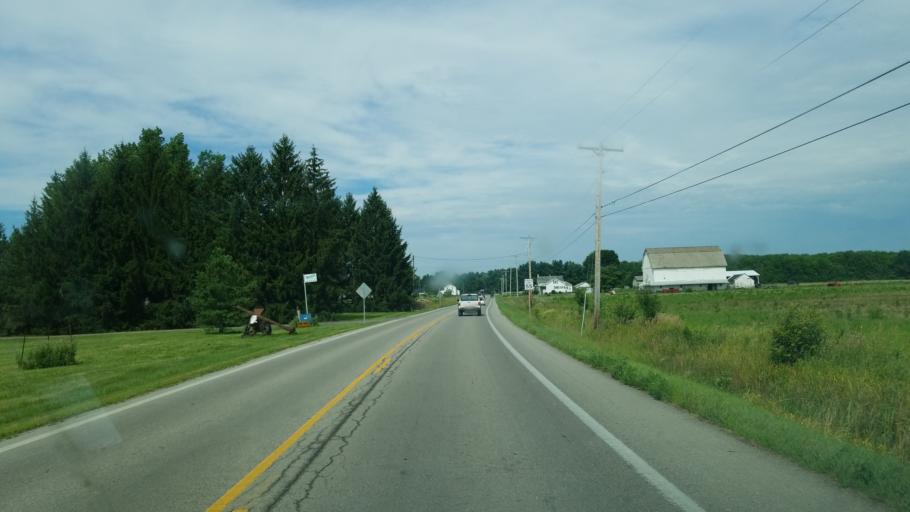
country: US
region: Ohio
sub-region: Ashland County
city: Ashland
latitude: 40.8808
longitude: -82.3518
